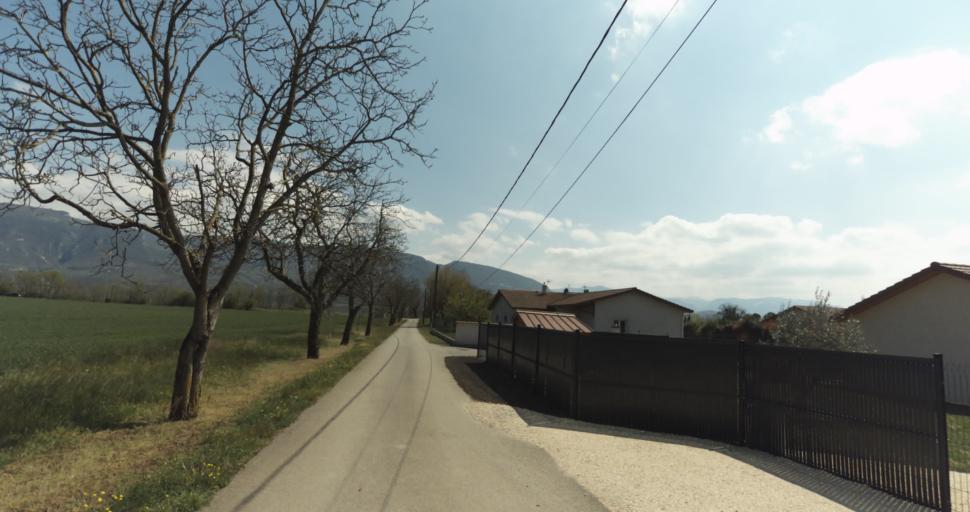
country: FR
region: Rhone-Alpes
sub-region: Departement de l'Isere
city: Saint-Romans
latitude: 45.1283
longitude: 5.3204
